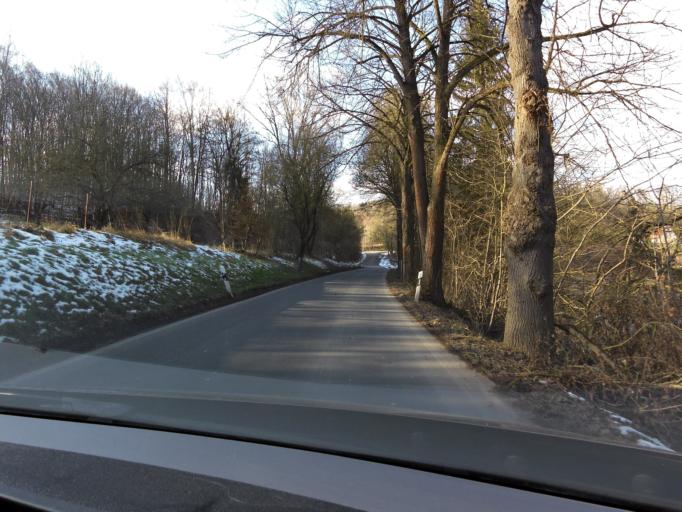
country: DE
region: Thuringia
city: Leimbach
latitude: 50.8418
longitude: 10.2063
